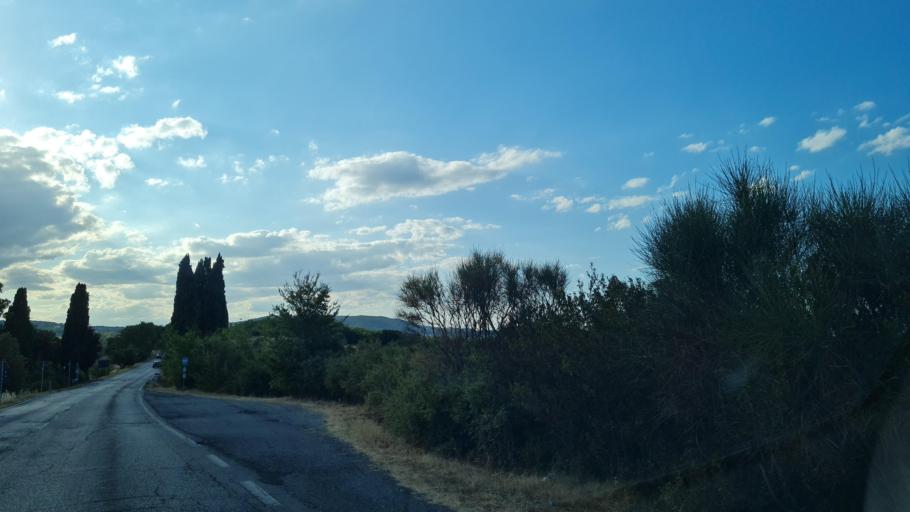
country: IT
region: Tuscany
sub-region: Provincia di Siena
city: Sarteano
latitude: 43.0291
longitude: 11.8638
